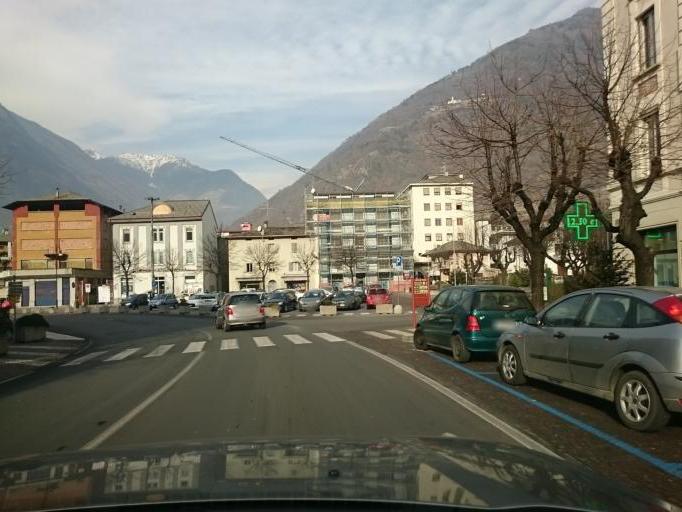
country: IT
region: Lombardy
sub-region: Provincia di Sondrio
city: Tirano
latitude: 46.2160
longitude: 10.1712
